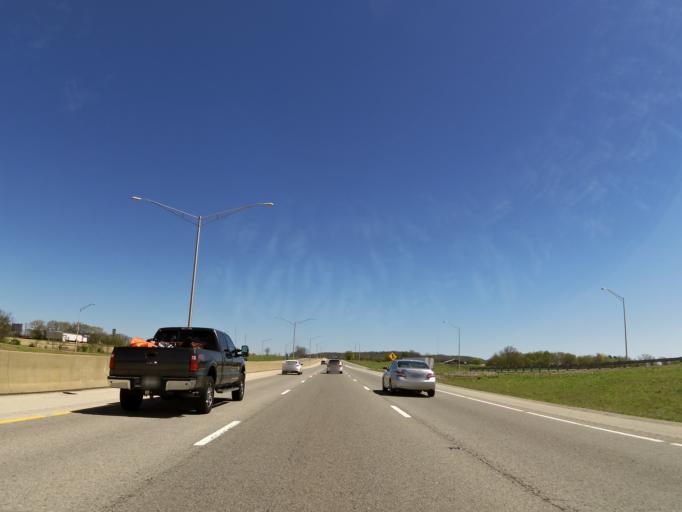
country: US
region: Kentucky
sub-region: Edmonson County
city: Brownsville
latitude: 37.0420
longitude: -86.2092
